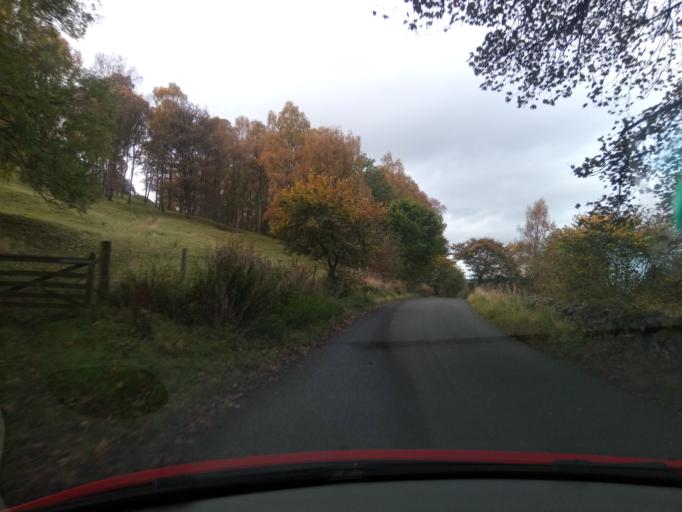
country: GB
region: Scotland
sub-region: The Scottish Borders
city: Peebles
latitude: 55.6403
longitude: -3.1519
